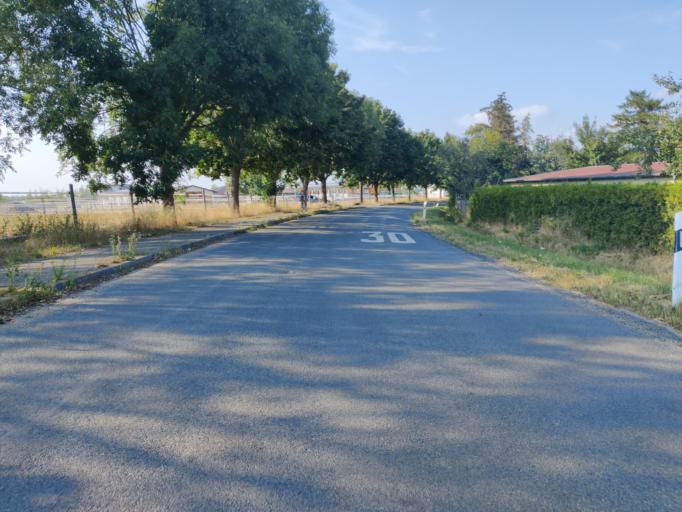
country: DE
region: Saxony
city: Neukieritzsch
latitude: 51.1652
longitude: 12.4326
